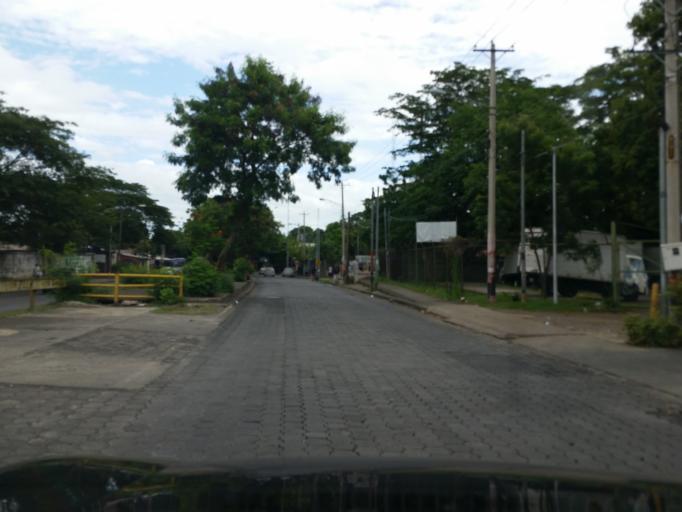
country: NI
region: Managua
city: Managua
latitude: 12.1456
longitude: -86.2242
